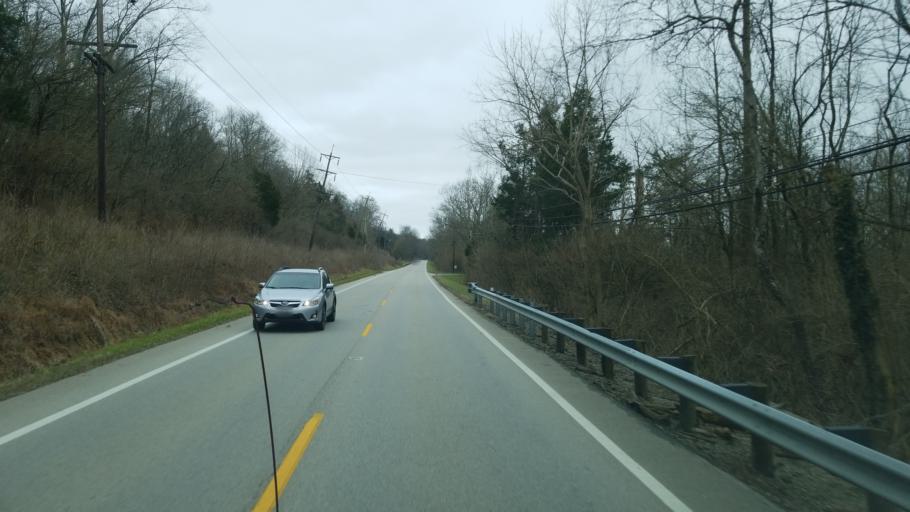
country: US
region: Ohio
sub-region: Clermont County
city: New Richmond
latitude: 38.8813
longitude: -84.2275
